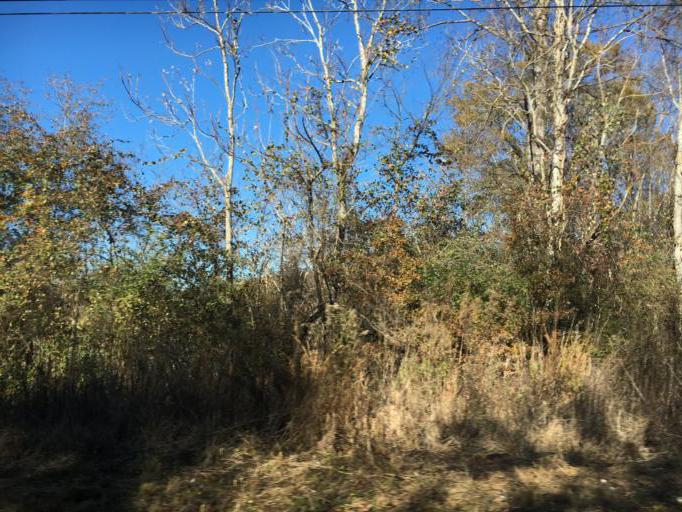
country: US
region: South Carolina
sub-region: Spartanburg County
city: Wellford
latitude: 34.8921
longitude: -82.0970
